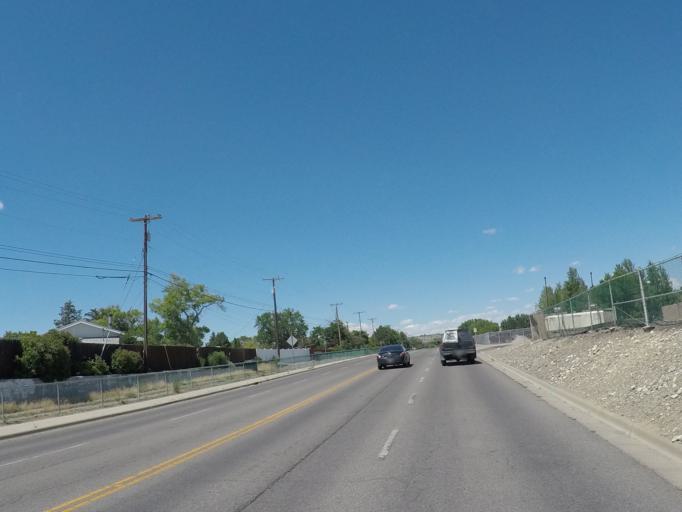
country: US
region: Montana
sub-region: Yellowstone County
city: Billings
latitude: 45.7643
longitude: -108.5650
